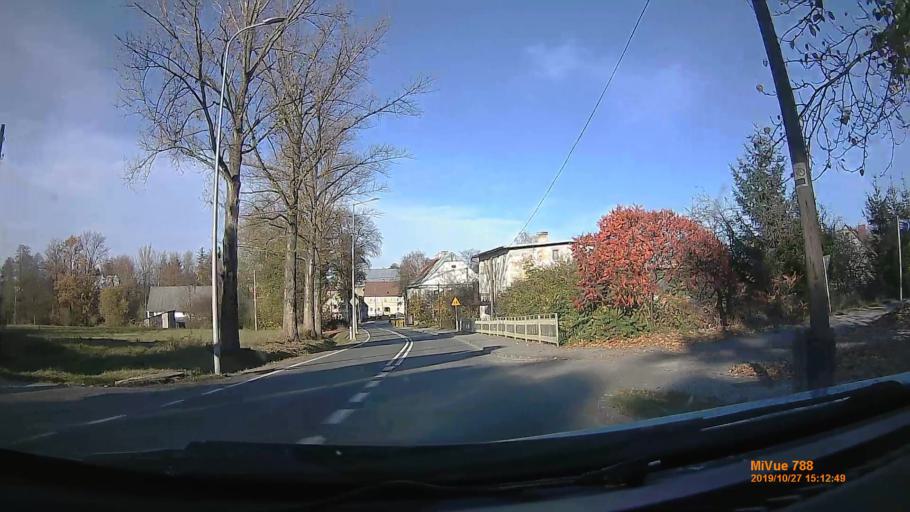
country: PL
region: Lower Silesian Voivodeship
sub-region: Powiat klodzki
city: Miedzylesie
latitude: 50.2127
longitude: 16.6794
